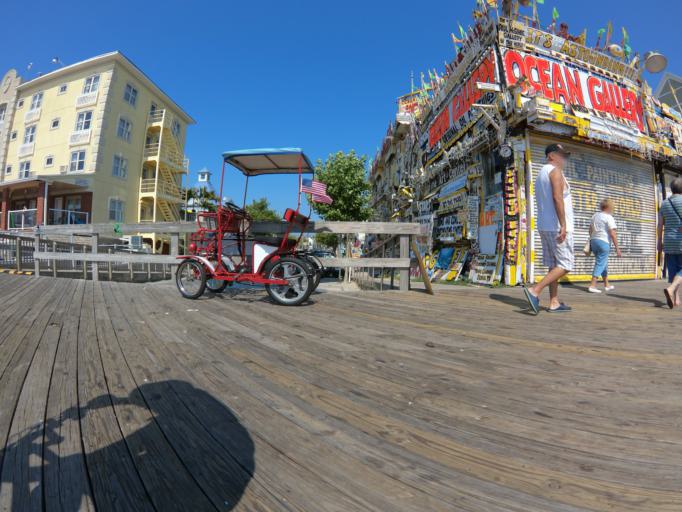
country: US
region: Maryland
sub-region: Worcester County
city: Ocean City
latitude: 38.3332
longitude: -75.0840
